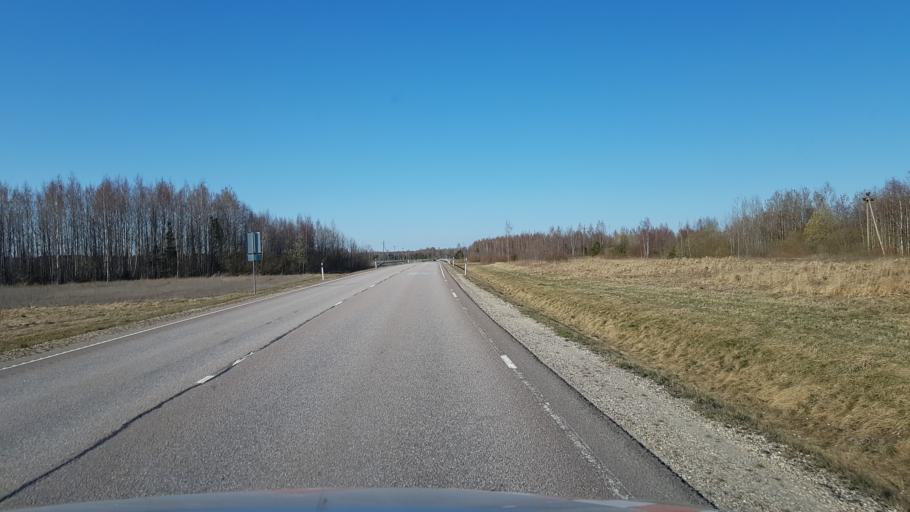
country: EE
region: Jogevamaa
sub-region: Mustvee linn
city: Mustvee
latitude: 58.8112
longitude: 26.9360
